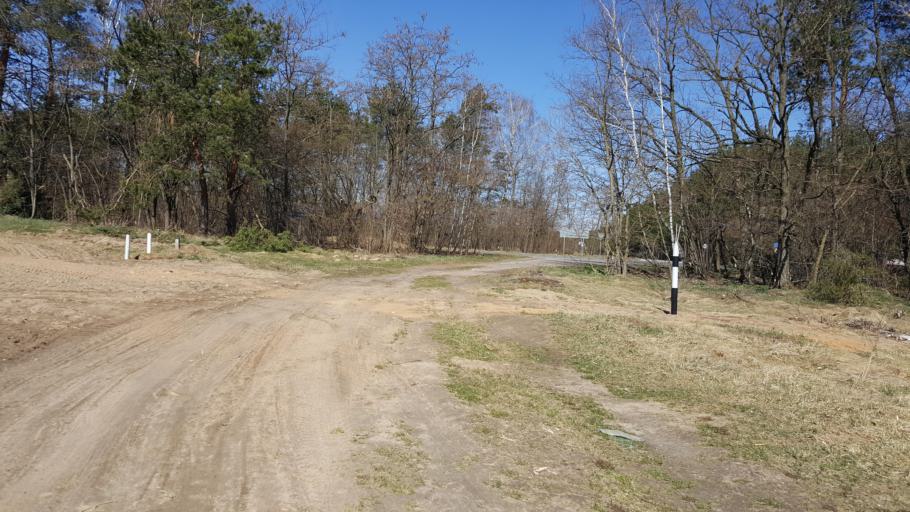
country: BY
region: Brest
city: Kamyanyets
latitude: 52.3302
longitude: 23.8284
